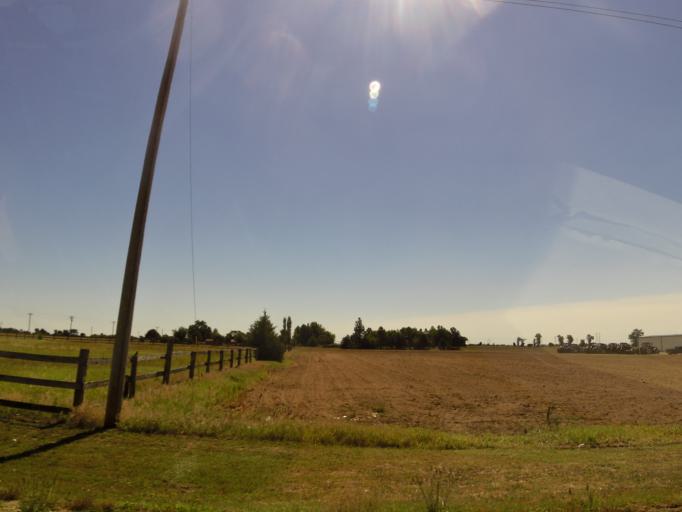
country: US
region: Missouri
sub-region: Dunklin County
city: Malden
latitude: 36.5262
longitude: -89.9707
